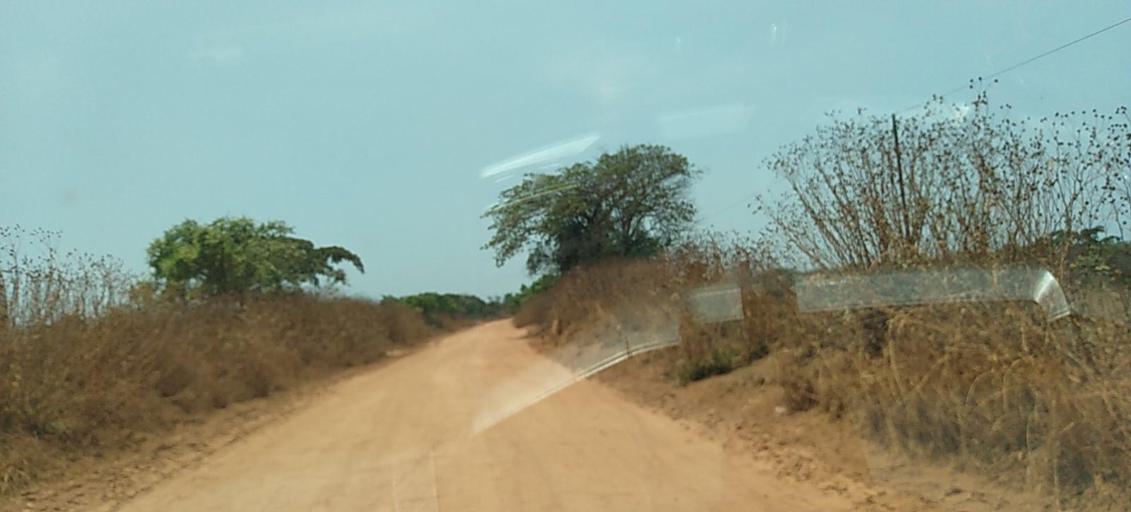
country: CD
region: Katanga
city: Kipushi
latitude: -11.7836
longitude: 27.1771
